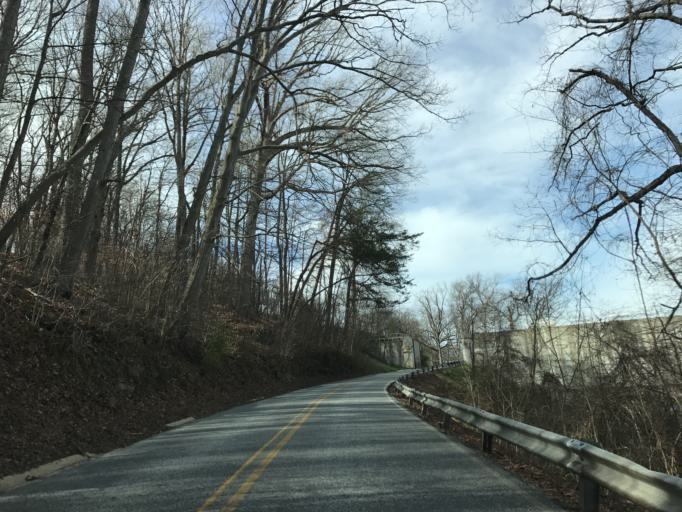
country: US
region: Maryland
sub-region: Baltimore County
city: Hampton
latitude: 39.4298
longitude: -76.5449
